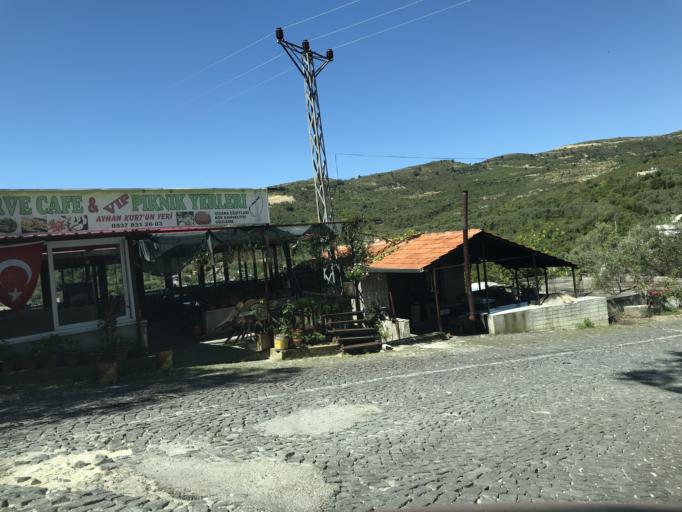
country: TR
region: Hatay
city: Samandag
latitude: 36.1321
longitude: 35.9763
